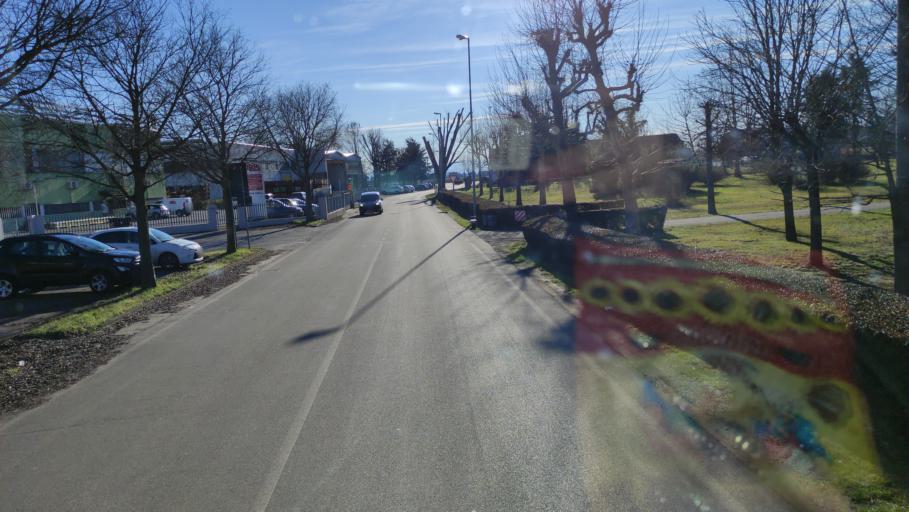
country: IT
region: Emilia-Romagna
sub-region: Provincia di Reggio Emilia
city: Campagnola Emilia
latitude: 44.8346
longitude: 10.7795
